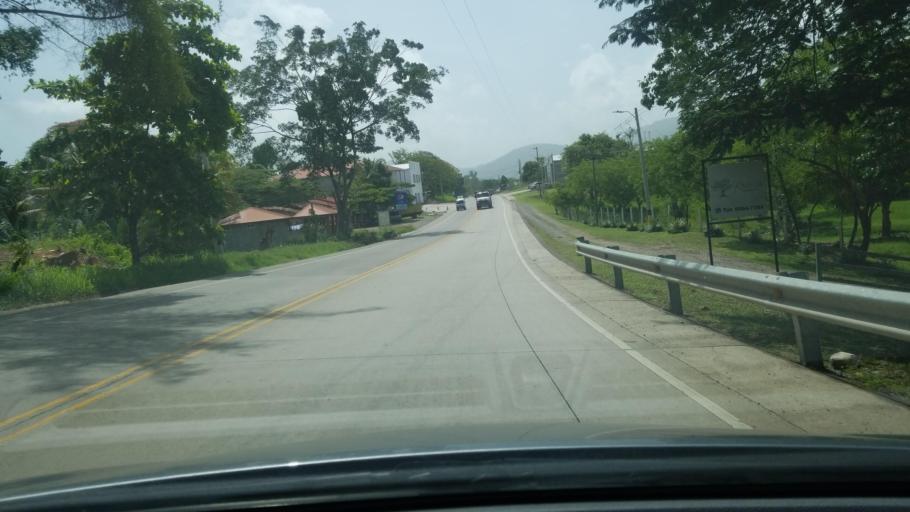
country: HN
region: Copan
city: La Entrada
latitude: 15.0693
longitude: -88.7725
